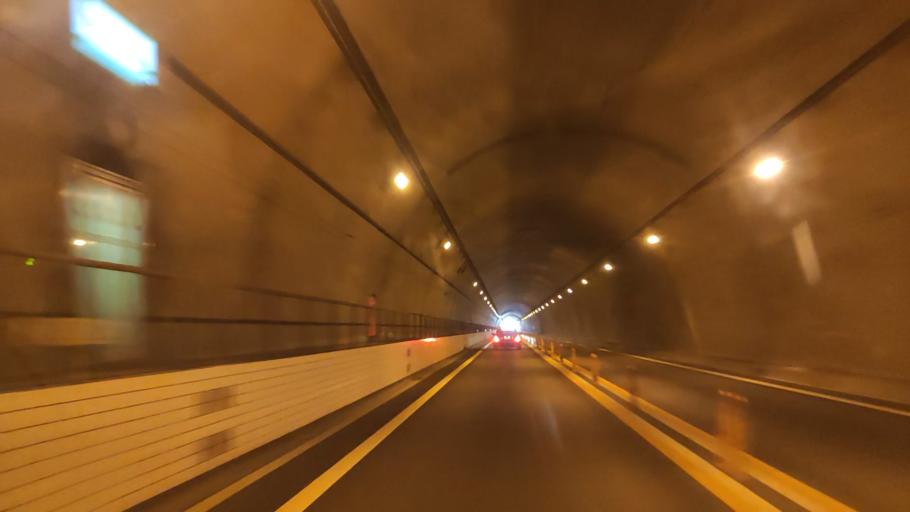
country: JP
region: Tokushima
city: Ikedacho
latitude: 34.0229
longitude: 133.7950
